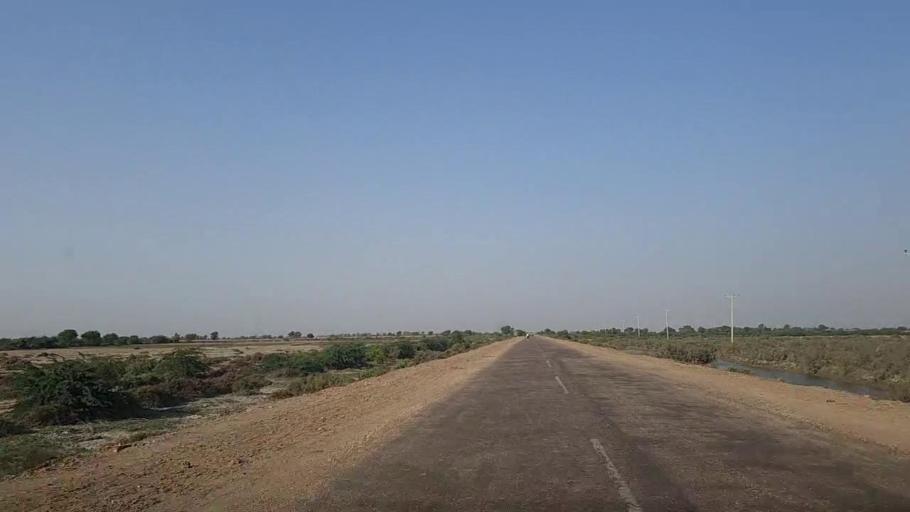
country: PK
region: Sindh
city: Mirpur Batoro
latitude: 24.6176
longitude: 68.4054
